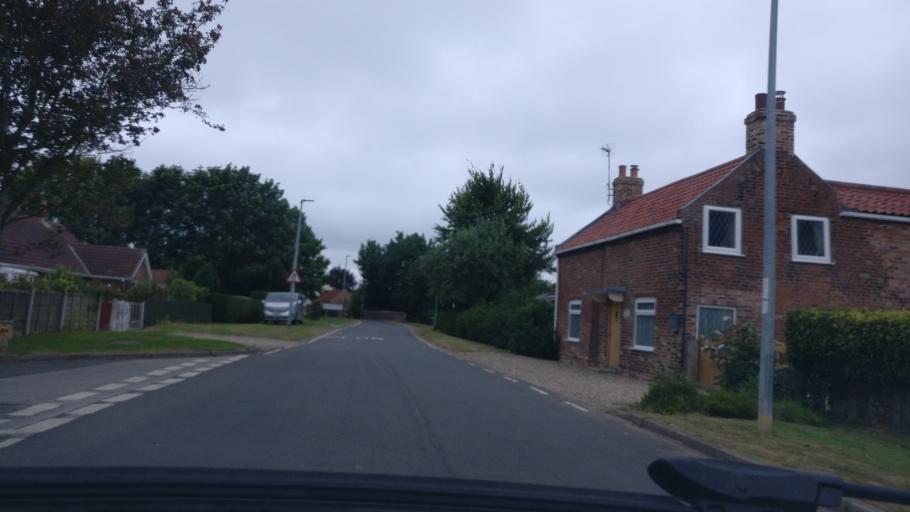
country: GB
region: England
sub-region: East Riding of Yorkshire
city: Leven
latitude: 53.8931
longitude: -0.3245
